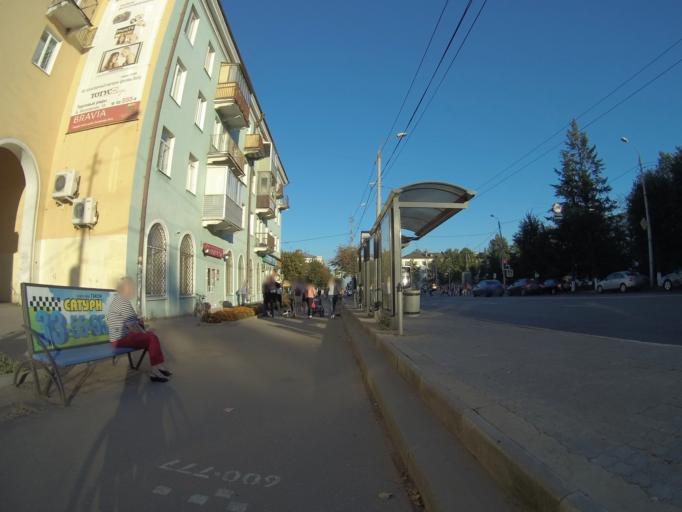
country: RU
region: Vladimir
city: Vladimir
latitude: 56.1436
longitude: 40.3878
